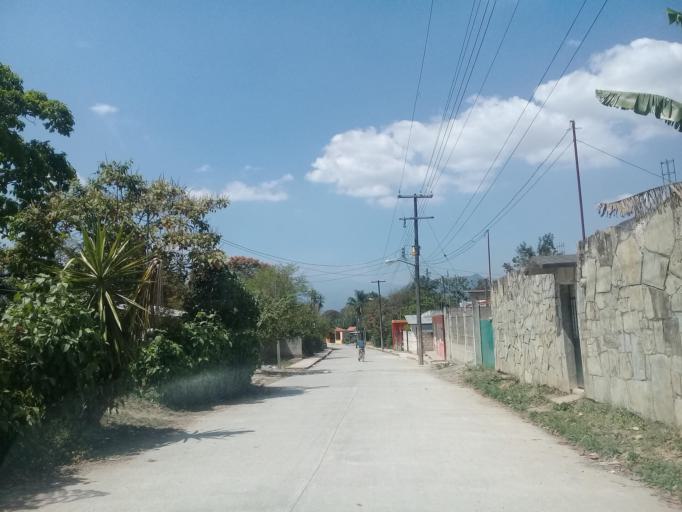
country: MX
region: Veracruz
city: Jalapilla
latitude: 18.8102
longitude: -97.0663
